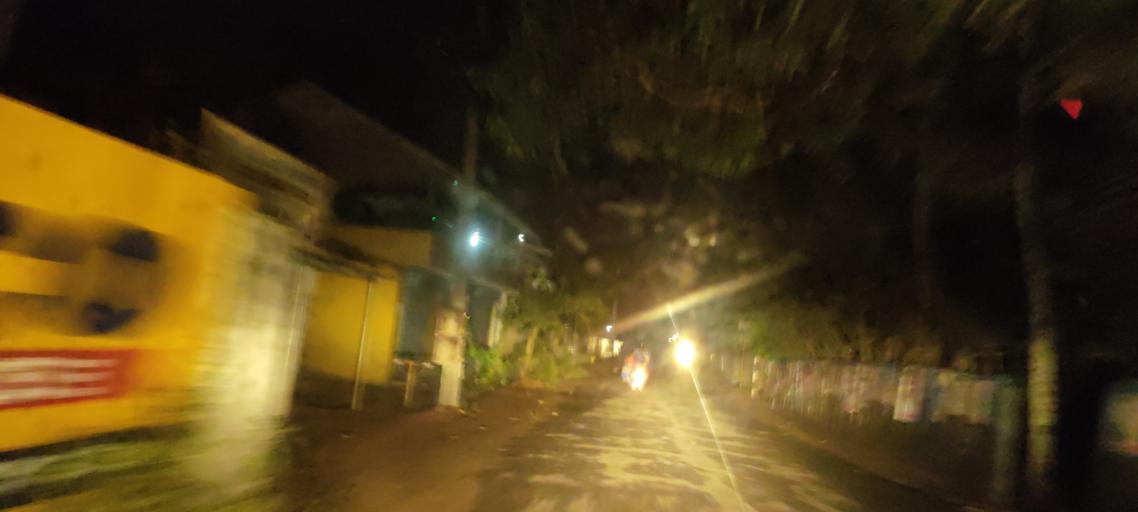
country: IN
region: Kerala
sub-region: Alappuzha
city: Vayalar
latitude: 9.7229
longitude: 76.3262
